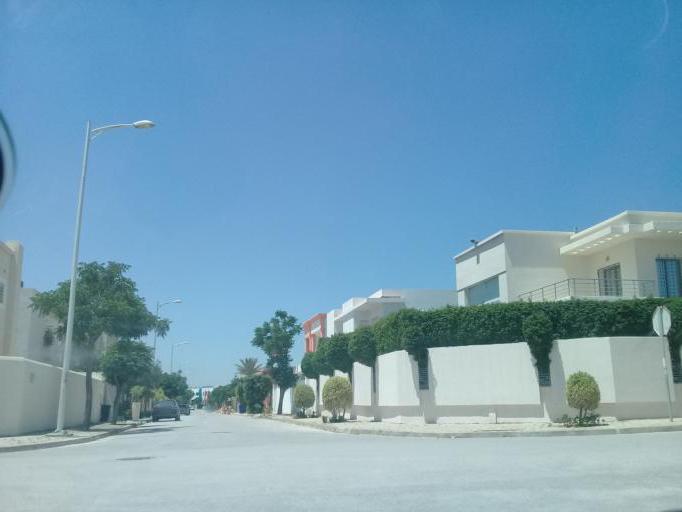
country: TN
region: Tunis
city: La Goulette
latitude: 36.8425
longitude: 10.2693
